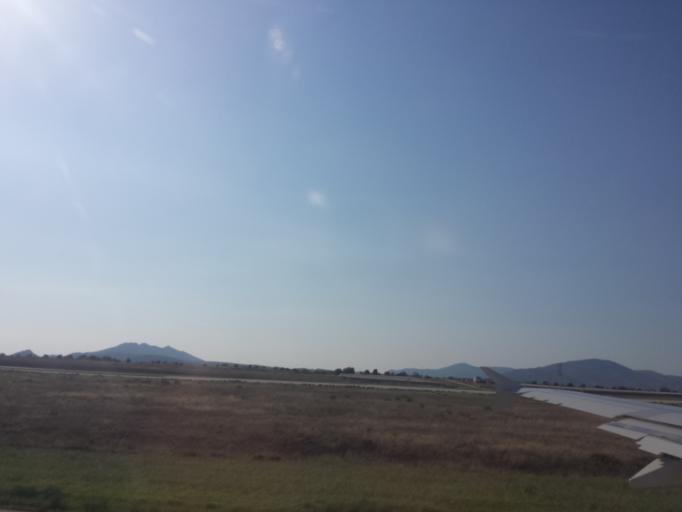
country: GR
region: Attica
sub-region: Nomarchia Anatolikis Attikis
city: Spata
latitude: 37.9302
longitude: 23.9468
